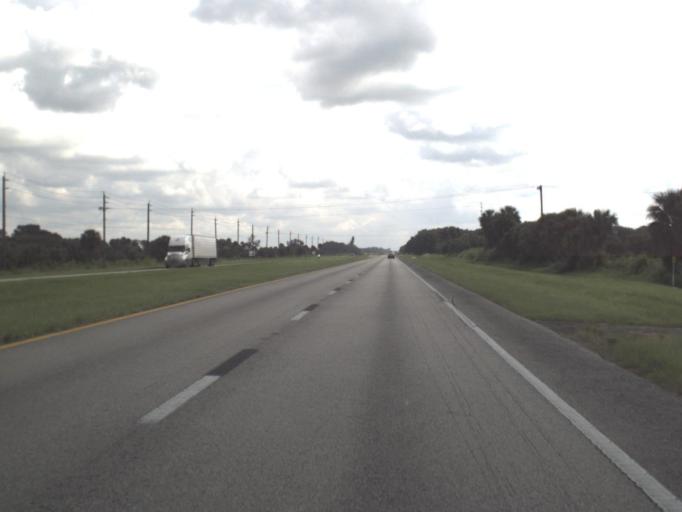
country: US
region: Florida
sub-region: Lee County
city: Alva
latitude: 26.7092
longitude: -81.5781
